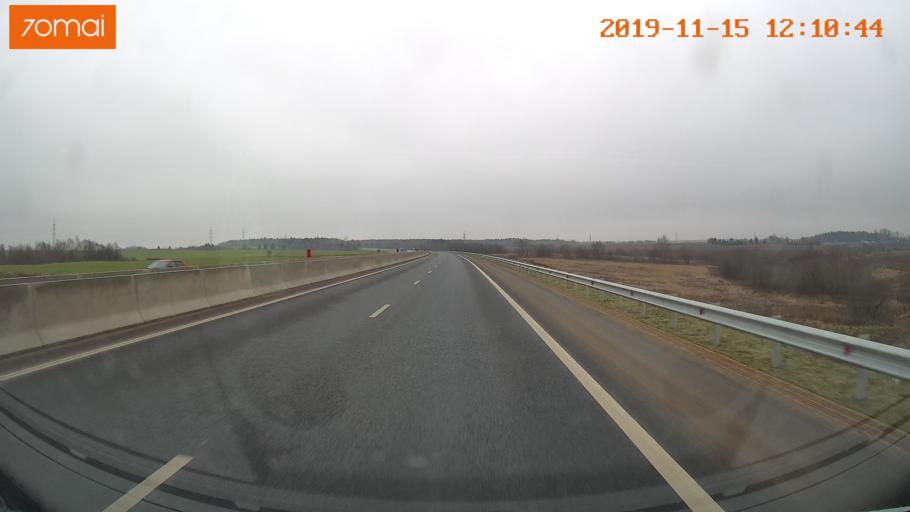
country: RU
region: Vologda
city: Molochnoye
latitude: 59.2002
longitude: 39.7590
